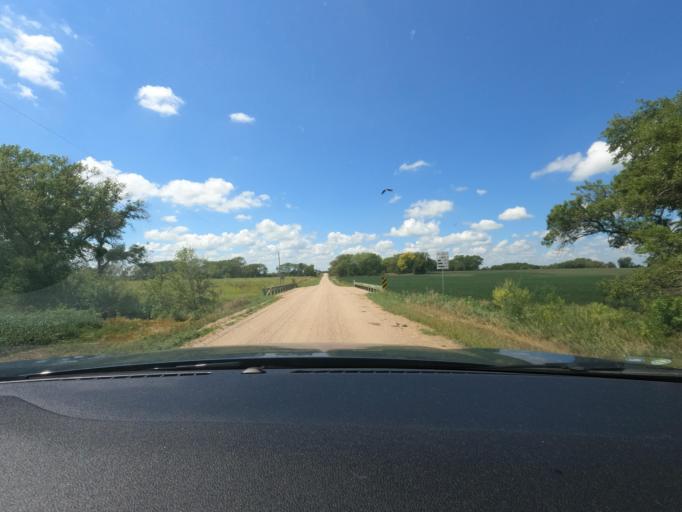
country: US
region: Nebraska
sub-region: Saunders County
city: Wahoo
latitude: 41.2491
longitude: -96.5447
